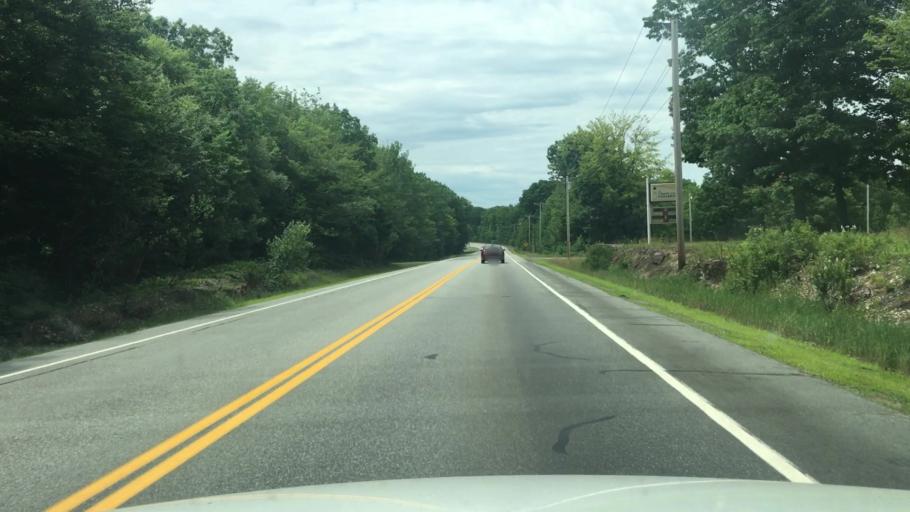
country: US
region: Maine
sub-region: Waldo County
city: Palermo
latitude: 44.4091
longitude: -69.5331
